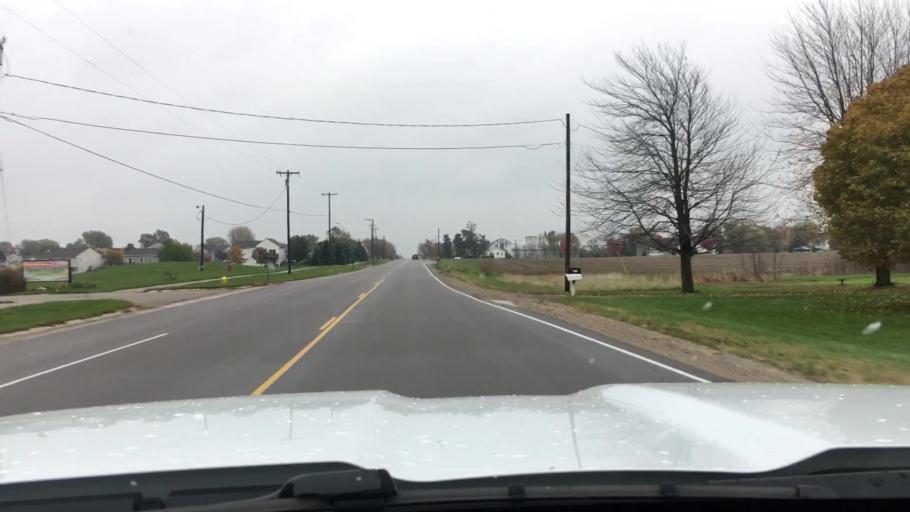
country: US
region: Michigan
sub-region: Ottawa County
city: Hudsonville
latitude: 42.8404
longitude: -85.8363
